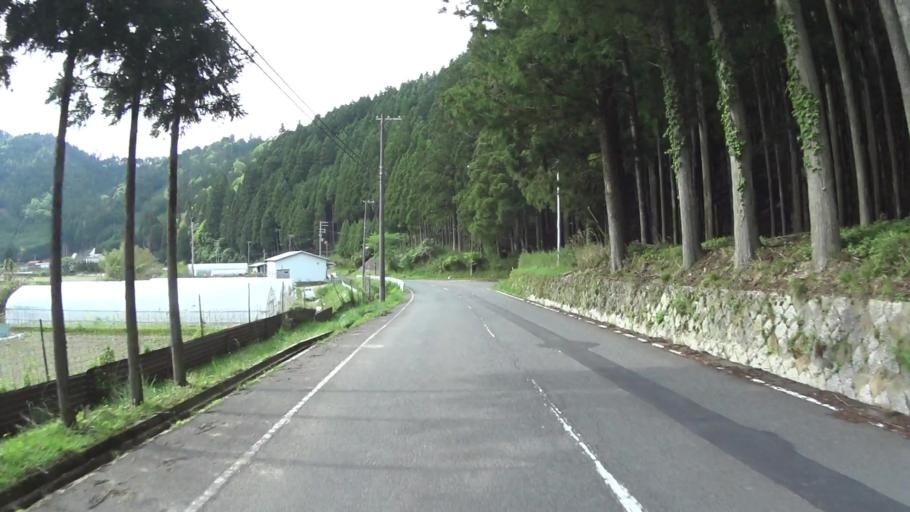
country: JP
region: Kyoto
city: Kameoka
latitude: 35.1213
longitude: 135.6069
